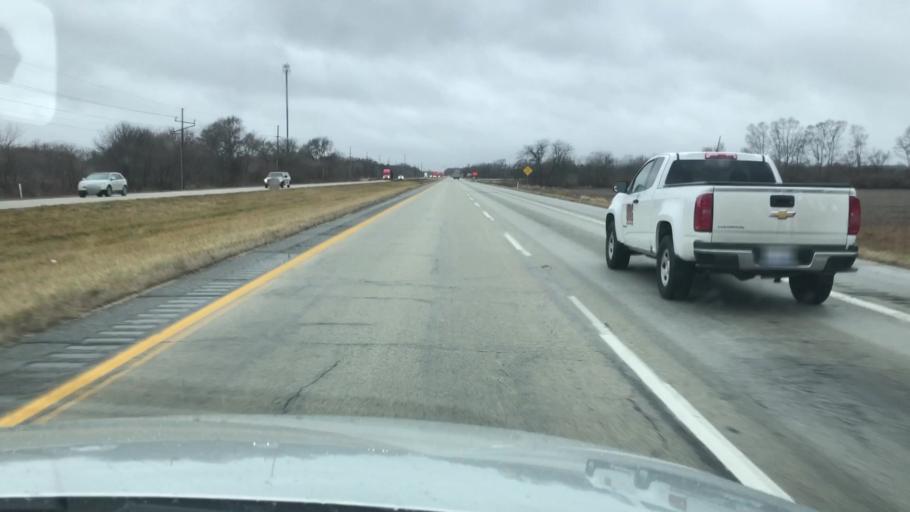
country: US
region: Indiana
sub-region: Starke County
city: Koontz Lake
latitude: 41.3768
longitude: -86.5407
